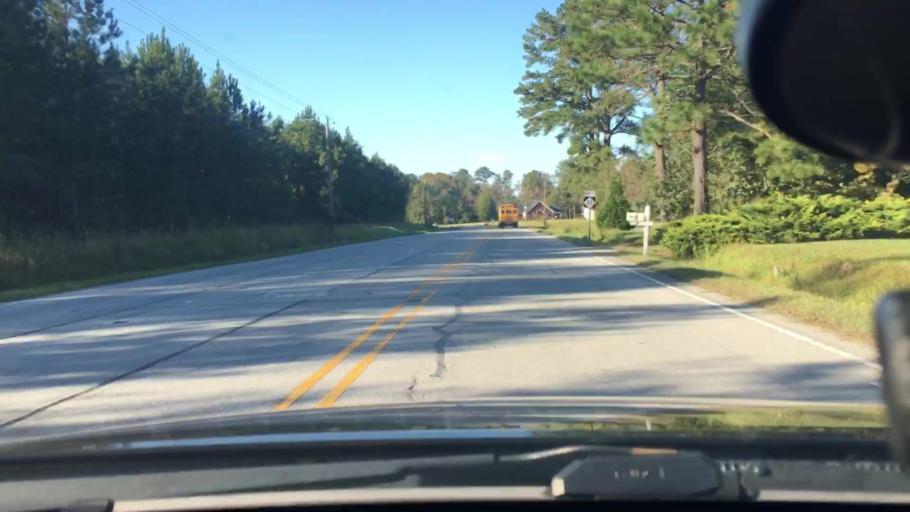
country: US
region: North Carolina
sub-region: Craven County
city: Vanceboro
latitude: 35.3326
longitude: -77.1719
